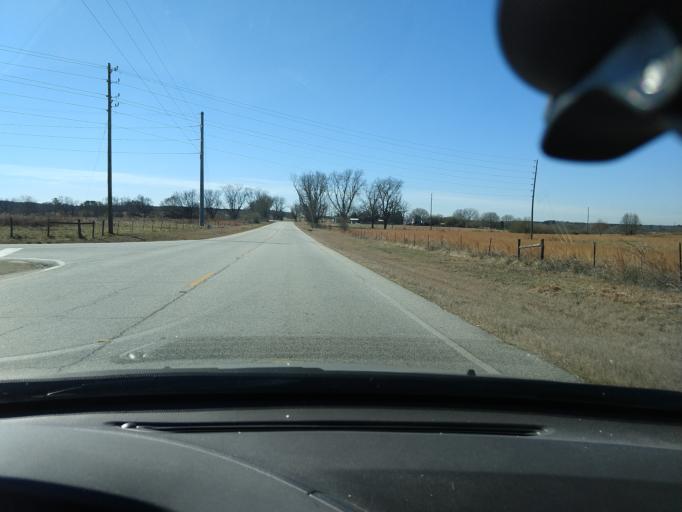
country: US
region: Georgia
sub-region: Newton County
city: Covington
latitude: 33.4903
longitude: -83.7407
